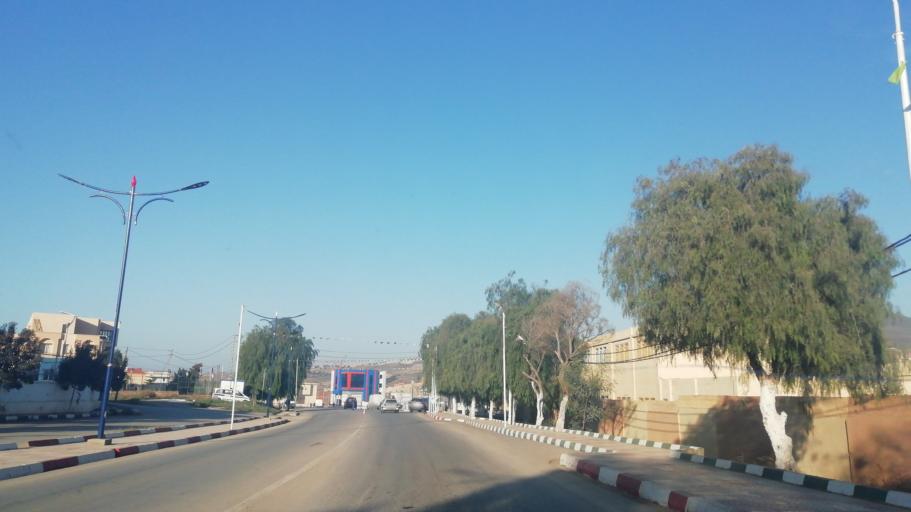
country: MA
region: Oriental
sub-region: Berkane-Taourirt
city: Ahfir
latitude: 34.9612
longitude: -2.0302
